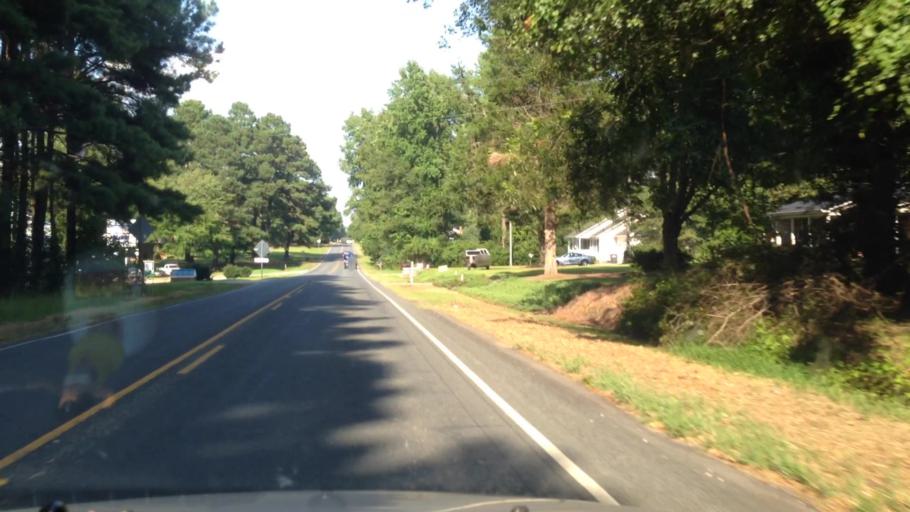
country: US
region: North Carolina
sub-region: Harnett County
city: Buies Creek
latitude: 35.4113
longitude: -78.7233
